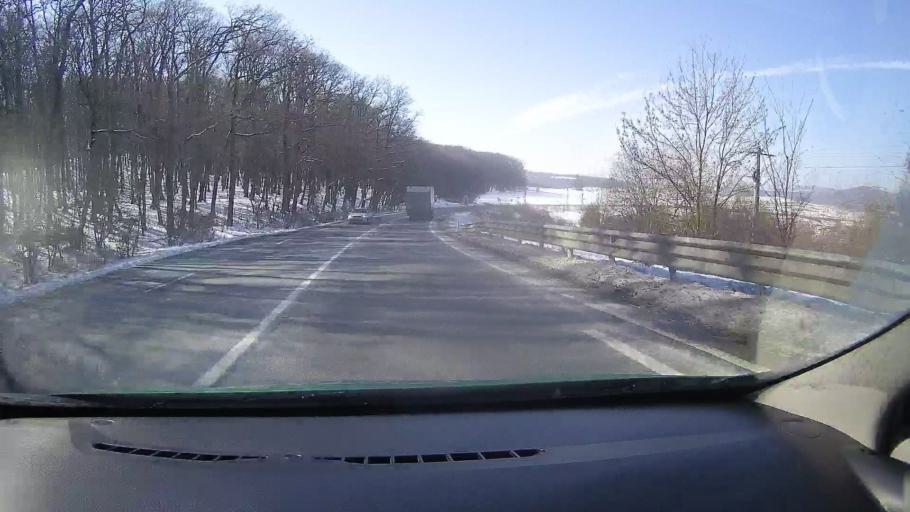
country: RO
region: Brasov
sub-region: Oras Rupea
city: Fiser
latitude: 46.0891
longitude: 25.1245
